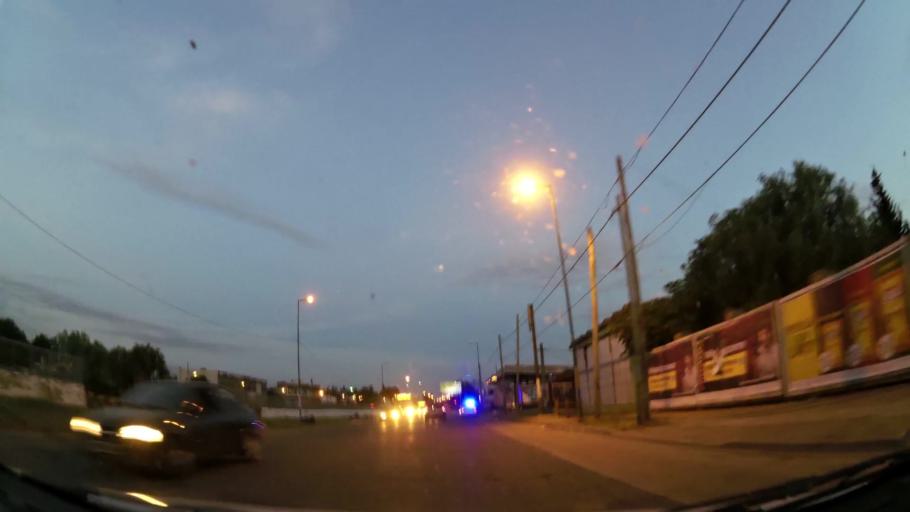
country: AR
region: Buenos Aires
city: Ituzaingo
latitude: -34.6639
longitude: -58.6833
